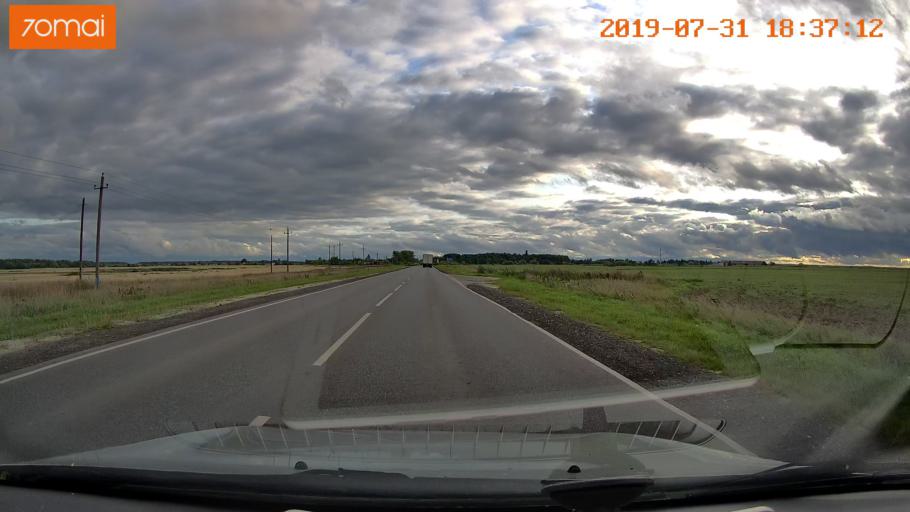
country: RU
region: Moskovskaya
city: Voskresensk
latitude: 55.2808
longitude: 38.6635
